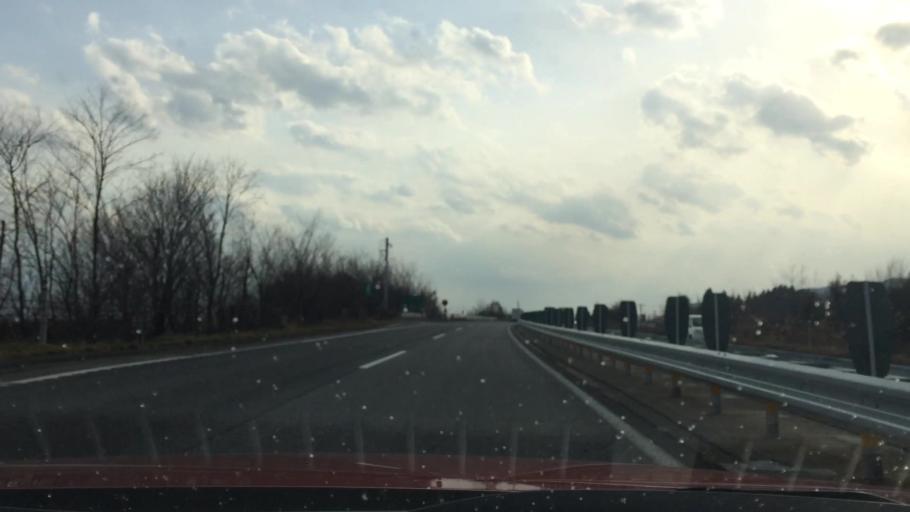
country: JP
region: Nagano
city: Iida
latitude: 35.6628
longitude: 137.9033
